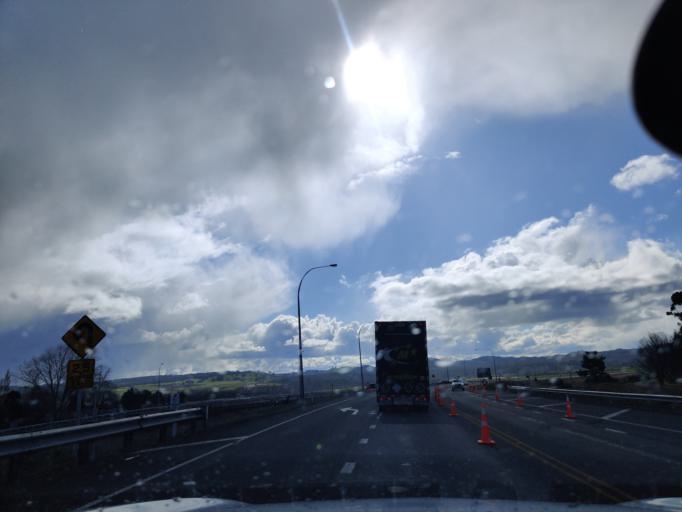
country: NZ
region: Waikato
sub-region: Taupo District
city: Taupo
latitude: -38.6683
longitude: 176.1038
